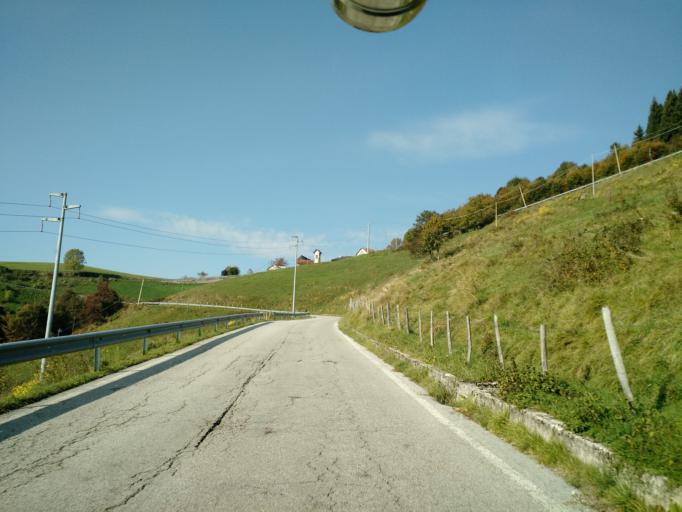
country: IT
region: Veneto
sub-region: Provincia di Vicenza
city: Foza
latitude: 45.8921
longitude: 11.5845
